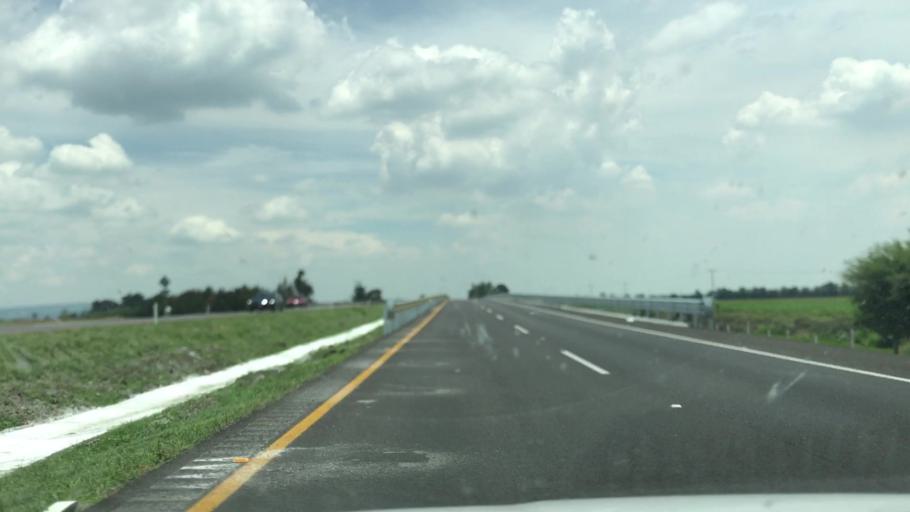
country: MX
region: Guanajuato
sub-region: Salamanca
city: San Vicente de Flores
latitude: 20.6315
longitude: -101.2516
